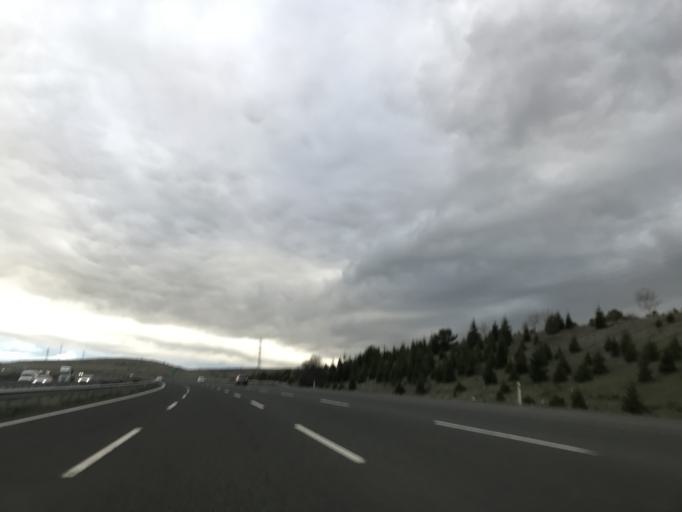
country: TR
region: Ankara
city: Etimesgut
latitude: 39.8025
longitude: 32.6453
